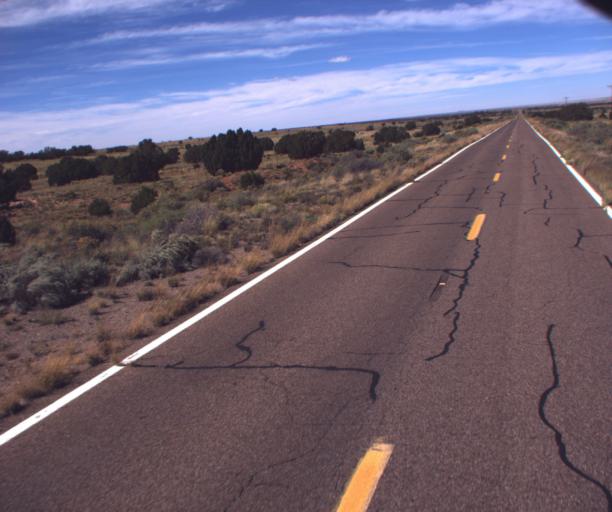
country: US
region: Arizona
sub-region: Apache County
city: Saint Johns
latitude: 34.5617
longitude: -109.6296
